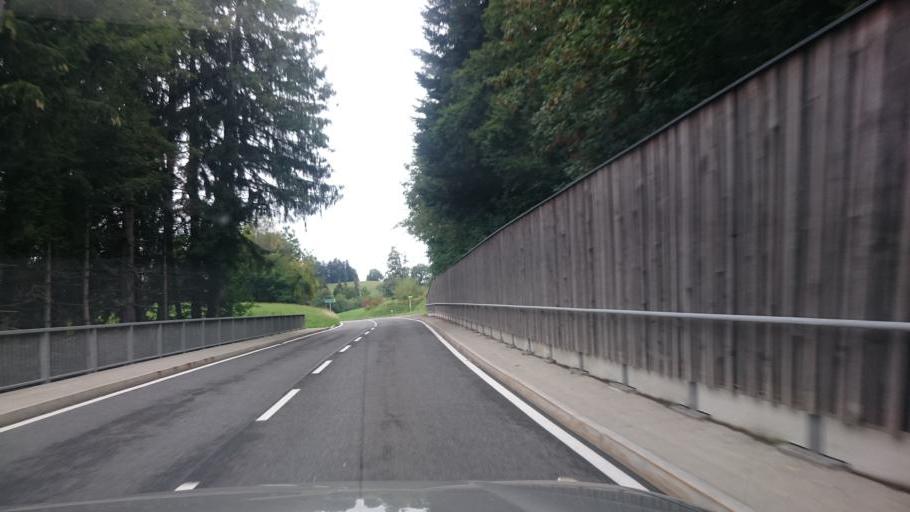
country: AT
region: Vorarlberg
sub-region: Politischer Bezirk Bregenz
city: Bildstein
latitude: 47.4268
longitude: 9.7788
